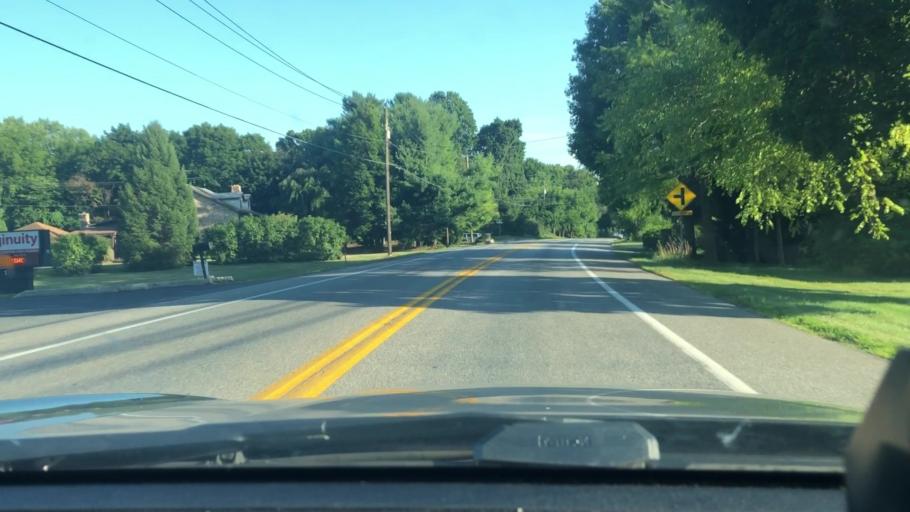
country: US
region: Pennsylvania
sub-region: Cumberland County
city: Mechanicsburg
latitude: 40.2345
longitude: -77.0067
